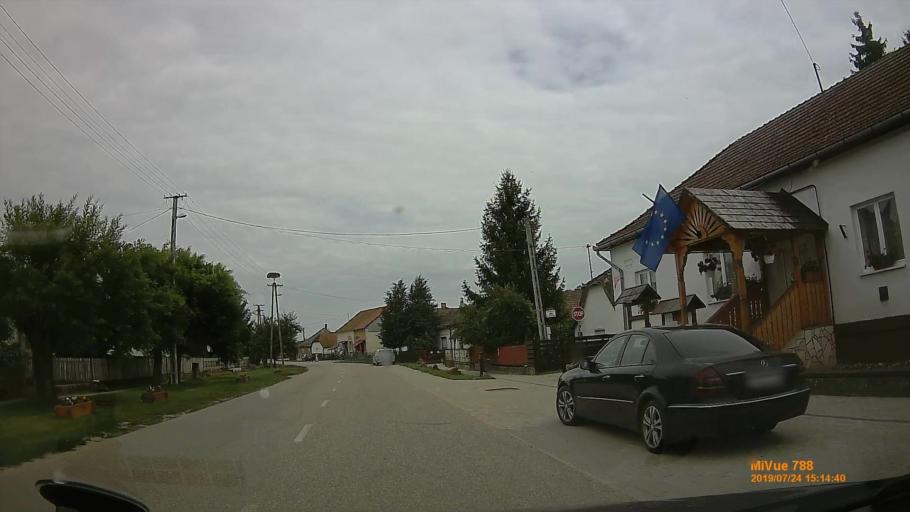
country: HU
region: Szabolcs-Szatmar-Bereg
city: Tarpa
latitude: 48.1988
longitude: 22.5256
